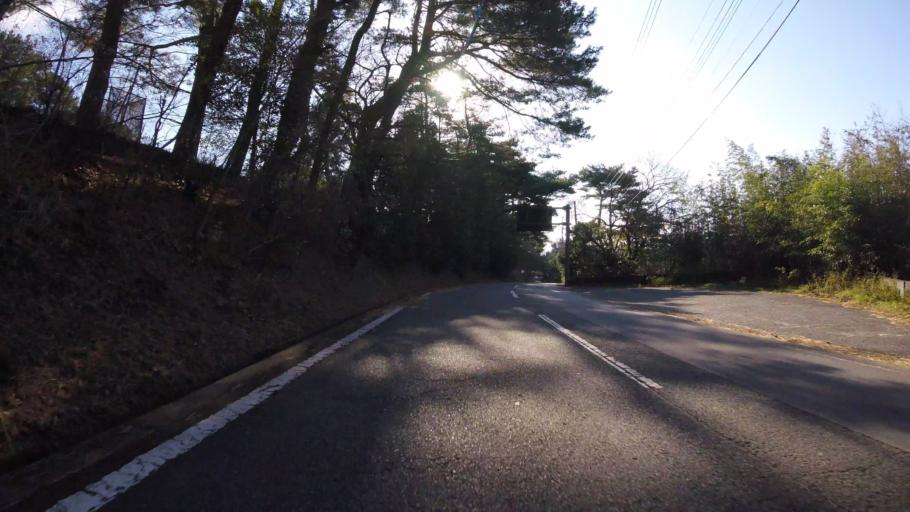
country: JP
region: Shizuoka
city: Atami
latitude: 35.1141
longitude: 139.0507
